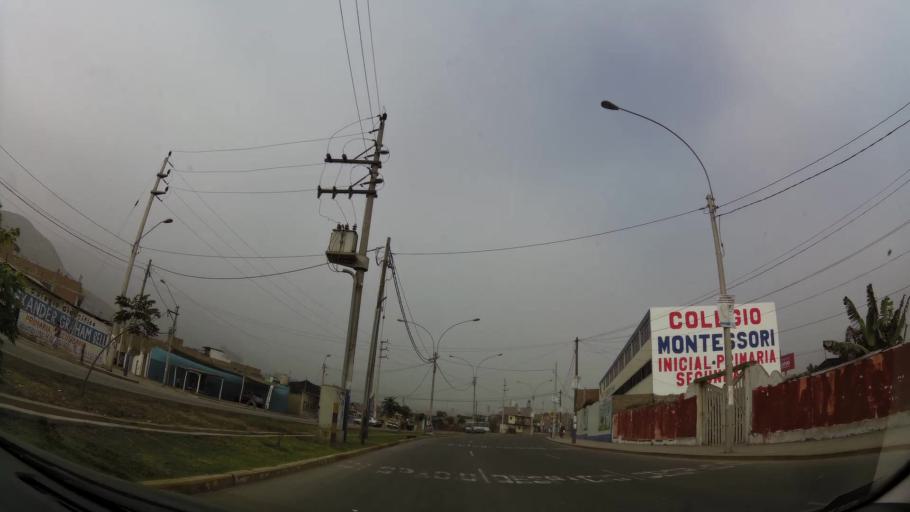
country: PE
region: Lima
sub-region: Lima
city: Santa Maria
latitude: -12.0041
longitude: -76.8314
